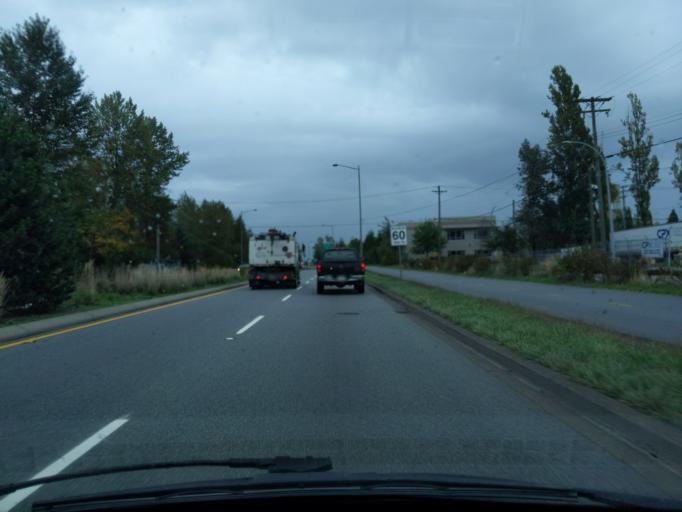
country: CA
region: British Columbia
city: Pitt Meadows
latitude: 49.1807
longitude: -122.6972
